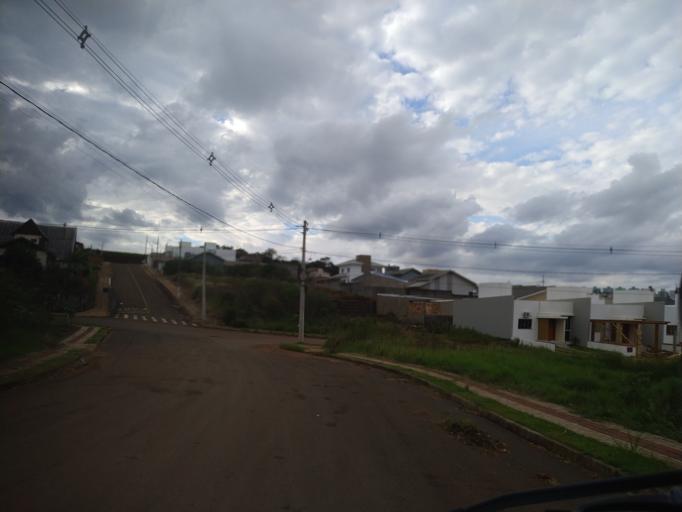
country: BR
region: Santa Catarina
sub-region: Chapeco
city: Chapeco
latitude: -27.0617
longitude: -52.6150
